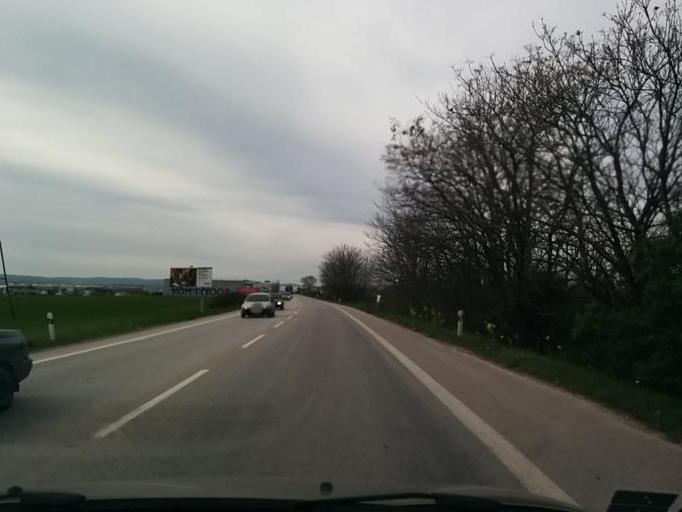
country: SK
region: Bratislavsky
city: Senec
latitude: 48.2281
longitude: 17.3788
